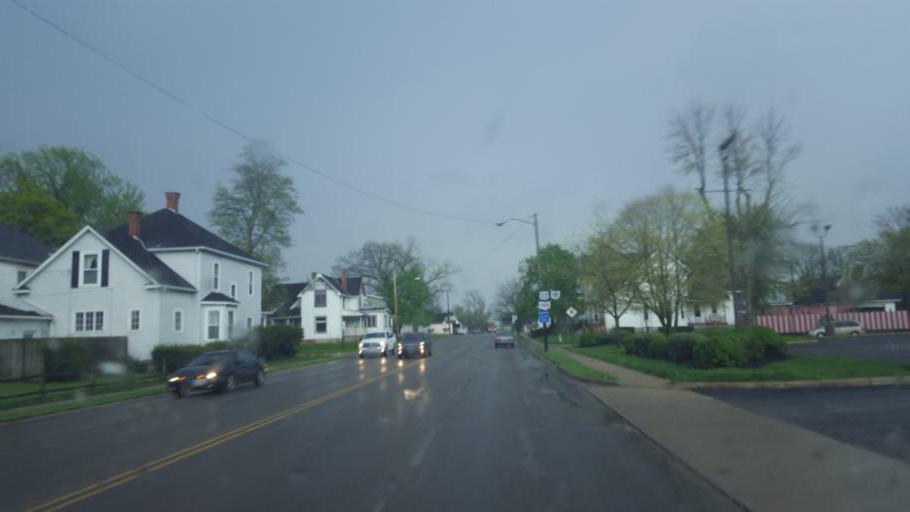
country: US
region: Ohio
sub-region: Seneca County
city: Fostoria
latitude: 41.1582
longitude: -83.4212
